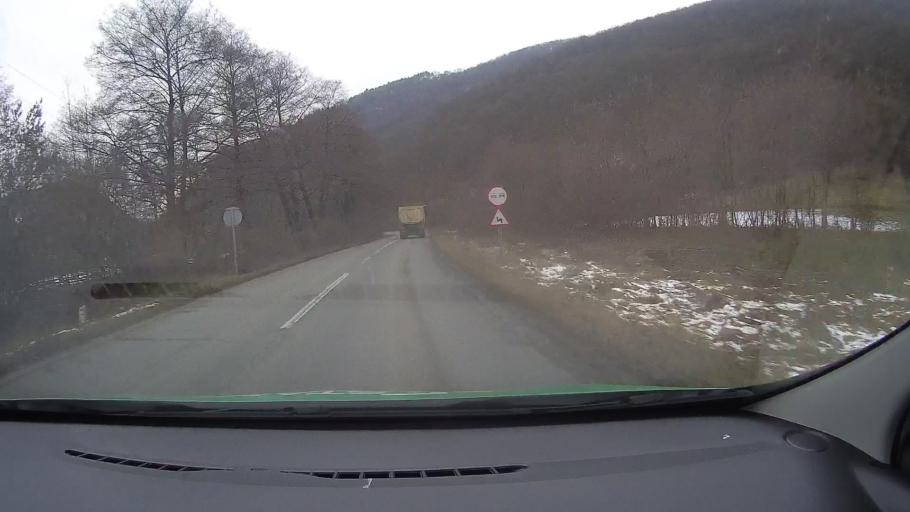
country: RO
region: Alba
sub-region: Comuna Metes
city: Metes
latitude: 46.0924
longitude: 23.3634
